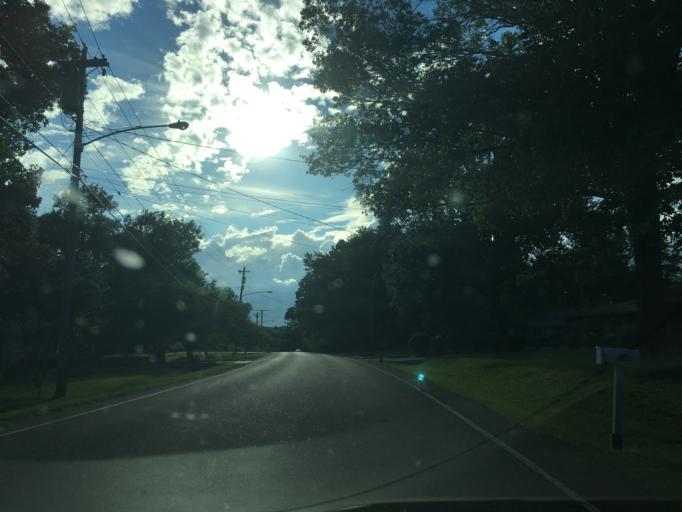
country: US
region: Tennessee
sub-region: Davidson County
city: Oak Hill
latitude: 36.0649
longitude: -86.7334
